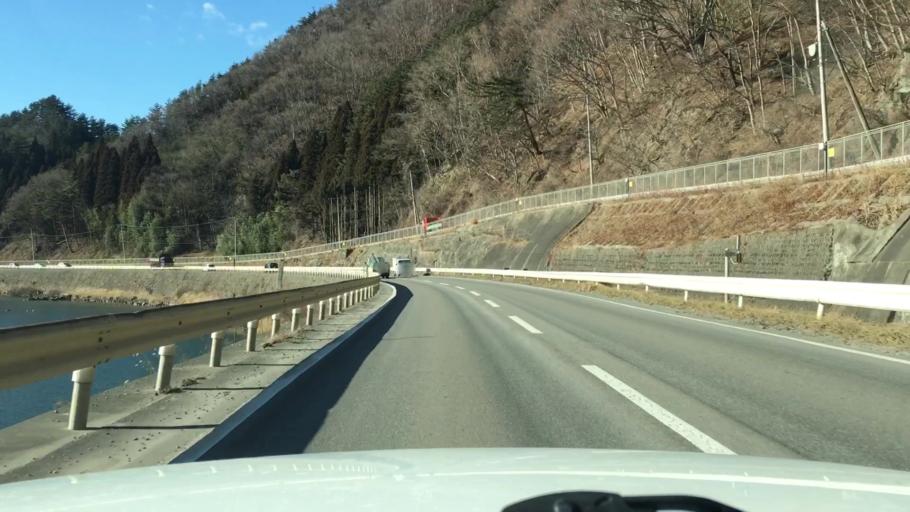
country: JP
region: Iwate
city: Miyako
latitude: 39.6356
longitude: 141.8469
